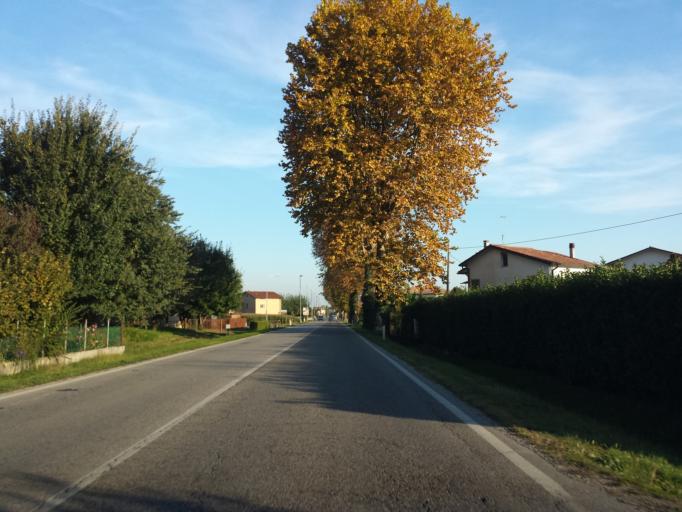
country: IT
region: Veneto
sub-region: Provincia di Vicenza
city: Motta
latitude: 45.6074
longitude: 11.4839
